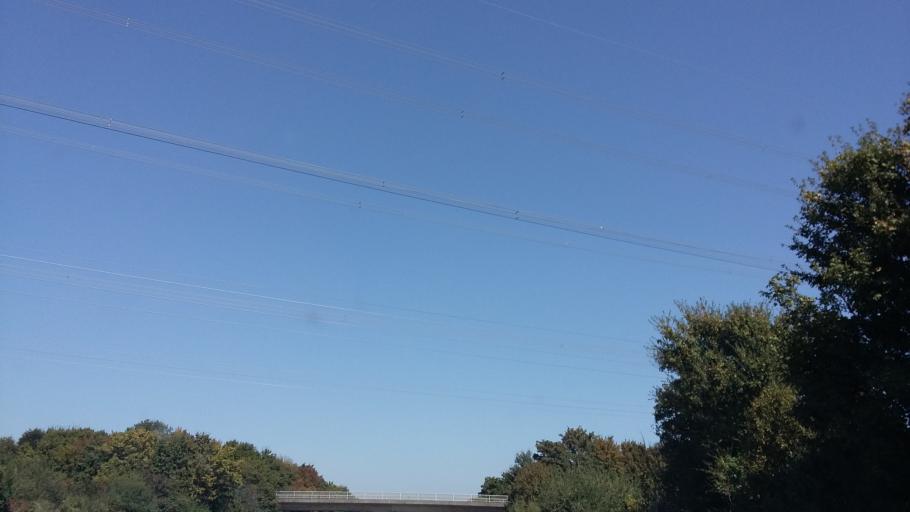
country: DE
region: Bavaria
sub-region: Swabia
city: Oberottmarshausen
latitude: 48.2317
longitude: 10.8673
